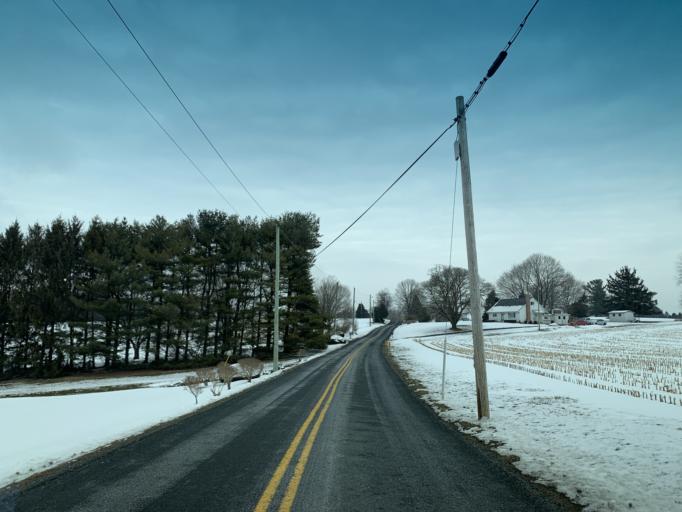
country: US
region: Pennsylvania
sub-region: York County
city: Susquehanna Trails
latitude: 39.7181
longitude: -76.2972
